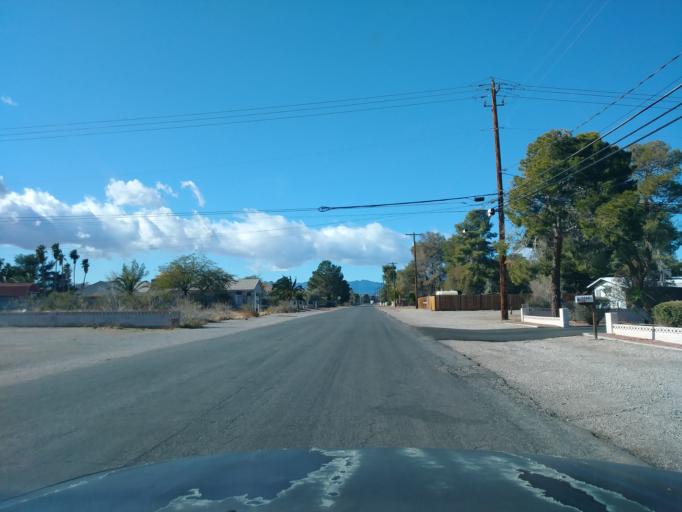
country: US
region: Nevada
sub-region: Clark County
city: Spring Valley
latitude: 36.1499
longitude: -115.2175
